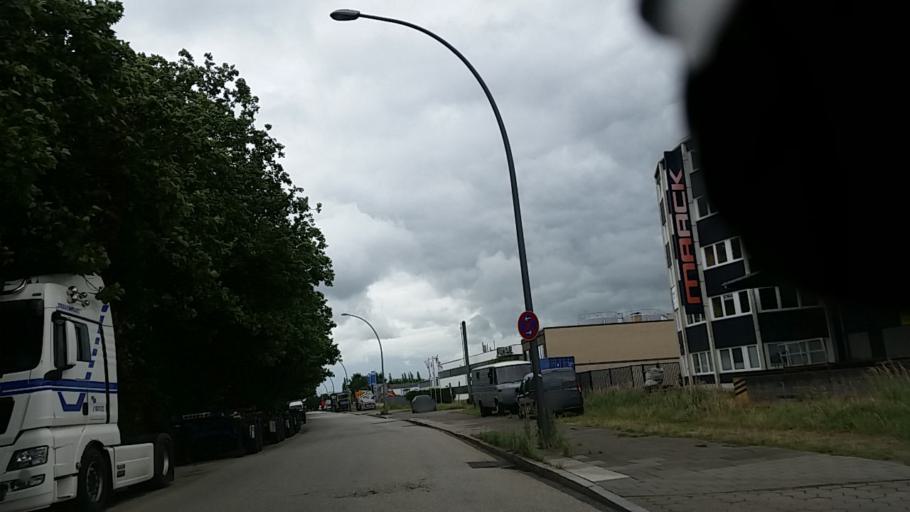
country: DE
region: Hamburg
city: Rothenburgsort
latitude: 53.5230
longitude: 10.0792
